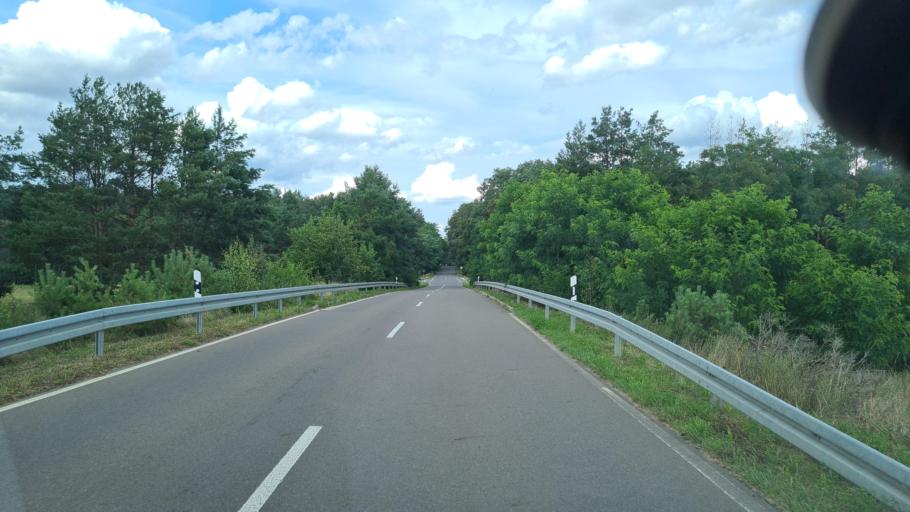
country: DE
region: Brandenburg
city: Drebkau
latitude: 51.6188
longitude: 14.2581
